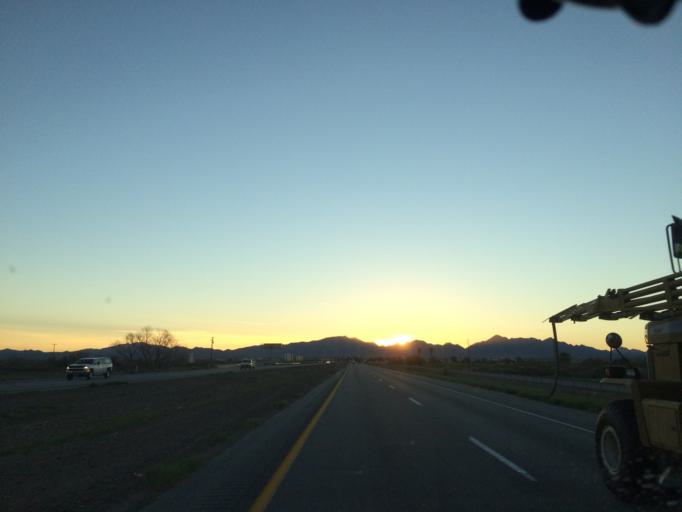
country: US
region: Arizona
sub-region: La Paz County
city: Ehrenberg
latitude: 33.6076
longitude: -114.5537
